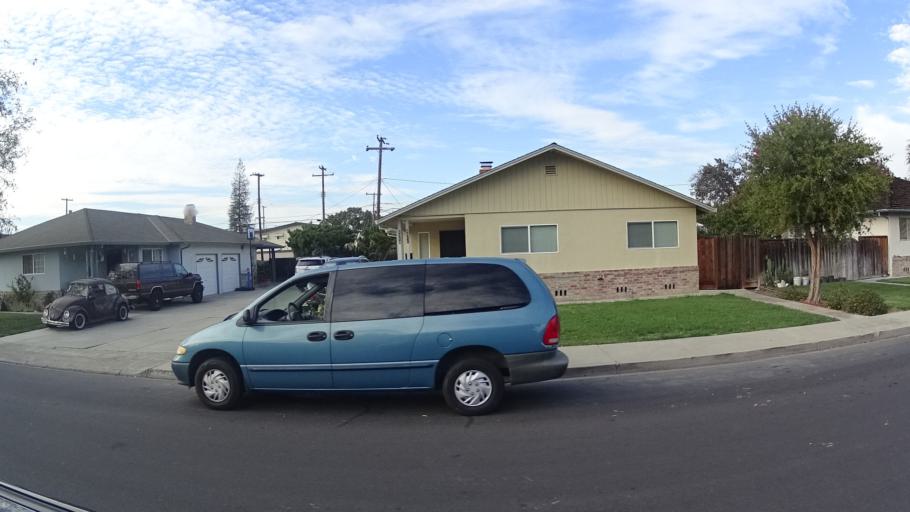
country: US
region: California
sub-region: Santa Clara County
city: Santa Clara
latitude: 37.3411
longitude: -121.9641
